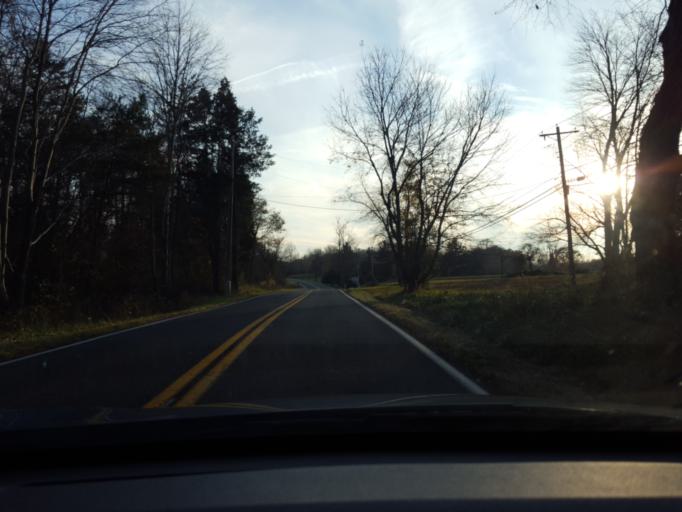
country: US
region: Maryland
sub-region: Charles County
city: Hughesville
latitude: 38.5039
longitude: -76.8664
